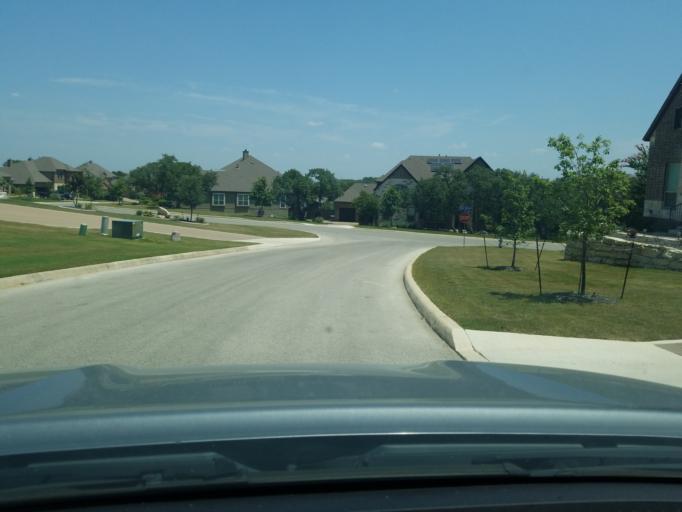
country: US
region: Texas
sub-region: Bexar County
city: Timberwood Park
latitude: 29.7098
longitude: -98.5070
